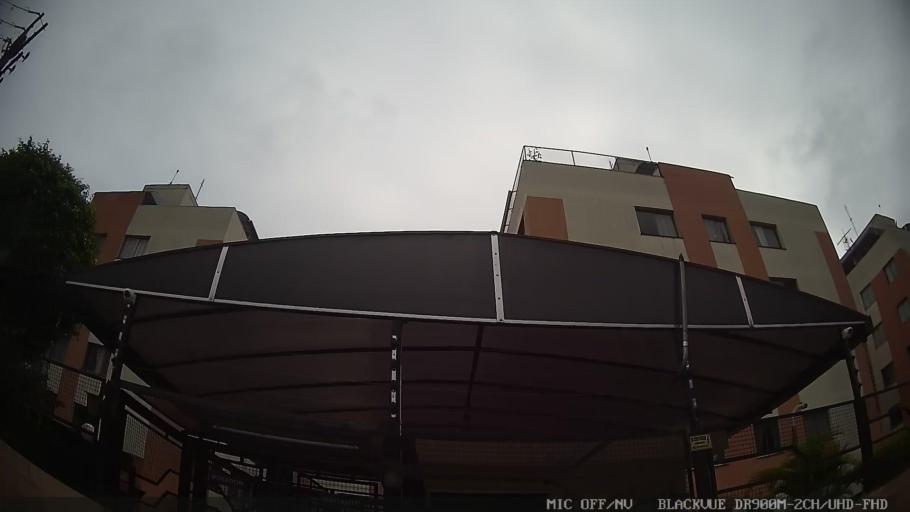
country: BR
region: Sao Paulo
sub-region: Osasco
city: Osasco
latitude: -23.4852
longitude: -46.7285
